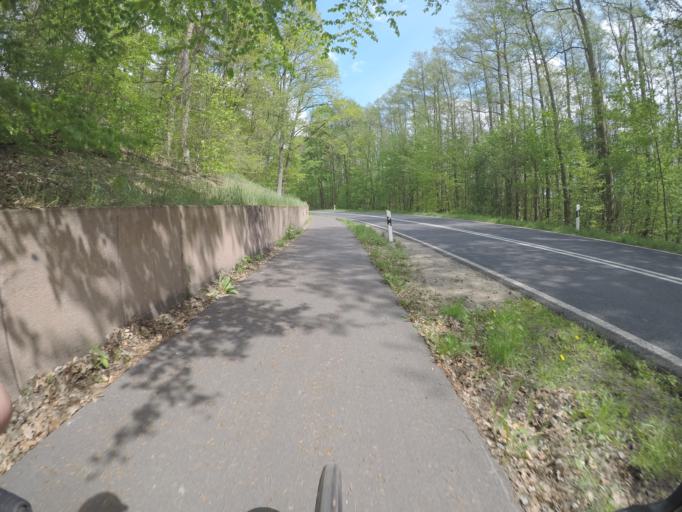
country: DE
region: Brandenburg
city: Joachimsthal
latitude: 52.9236
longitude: 13.7035
